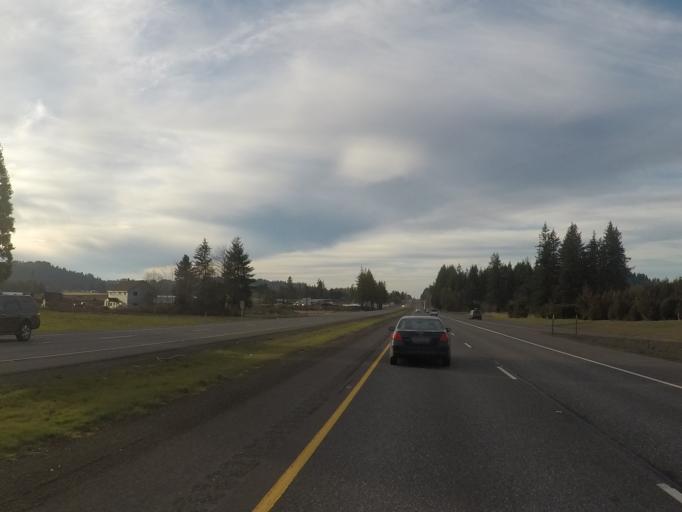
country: US
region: Oregon
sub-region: Clackamas County
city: Sandy
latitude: 45.4338
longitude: -122.3450
